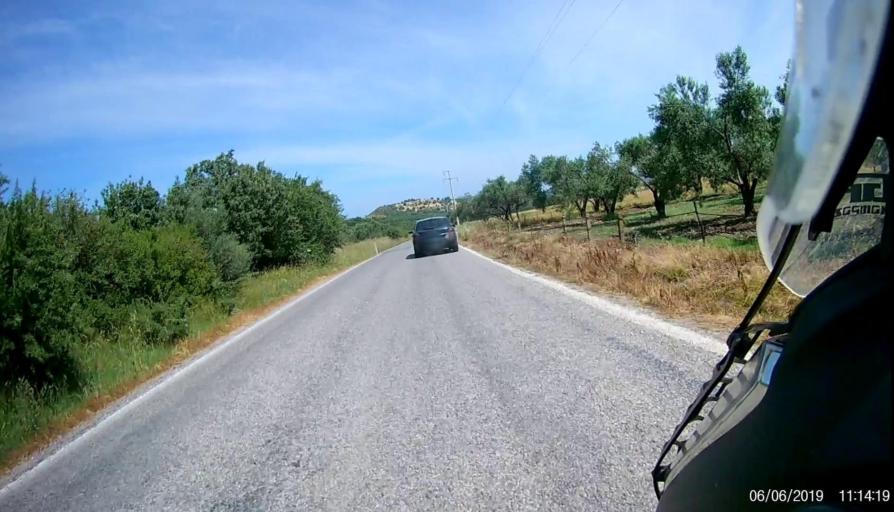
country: TR
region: Canakkale
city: Gulpinar
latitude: 39.6229
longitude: 26.1751
